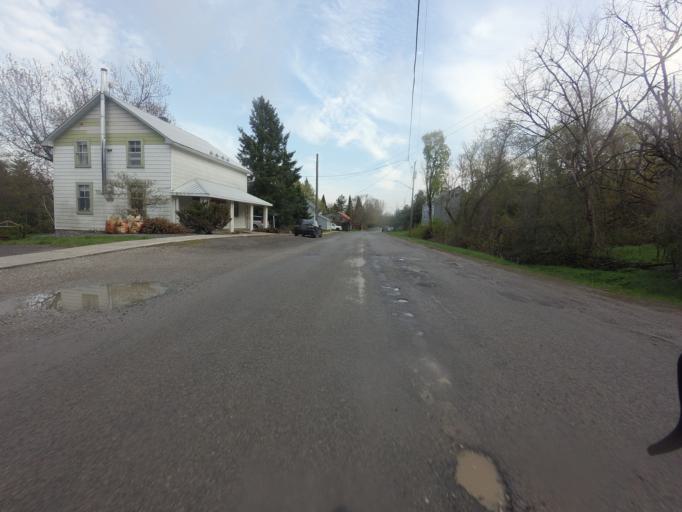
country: CA
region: Ontario
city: Carleton Place
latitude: 45.1936
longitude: -76.3262
